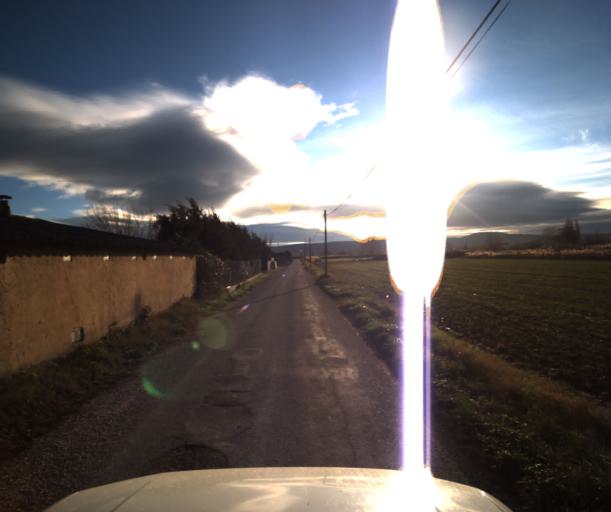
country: FR
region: Provence-Alpes-Cote d'Azur
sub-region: Departement du Vaucluse
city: Pertuis
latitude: 43.6858
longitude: 5.4949
